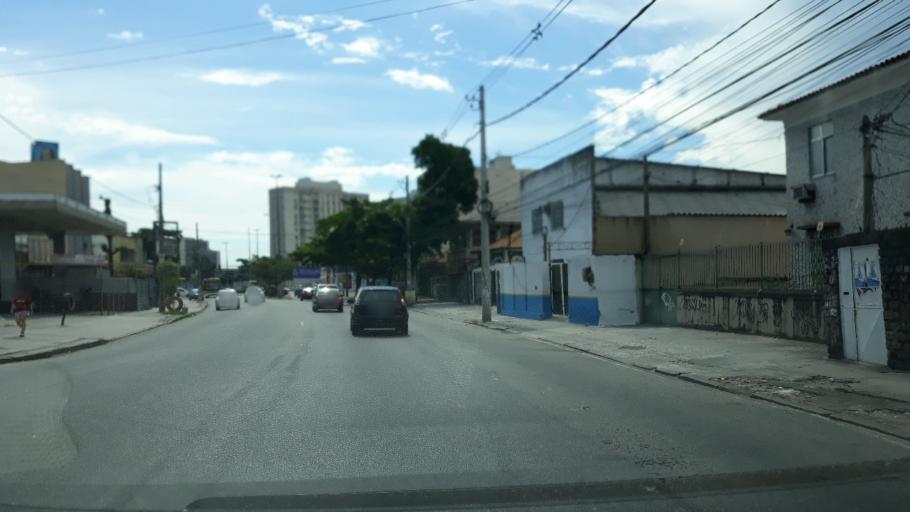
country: BR
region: Rio de Janeiro
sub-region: Rio De Janeiro
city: Rio de Janeiro
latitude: -22.8781
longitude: -43.2626
